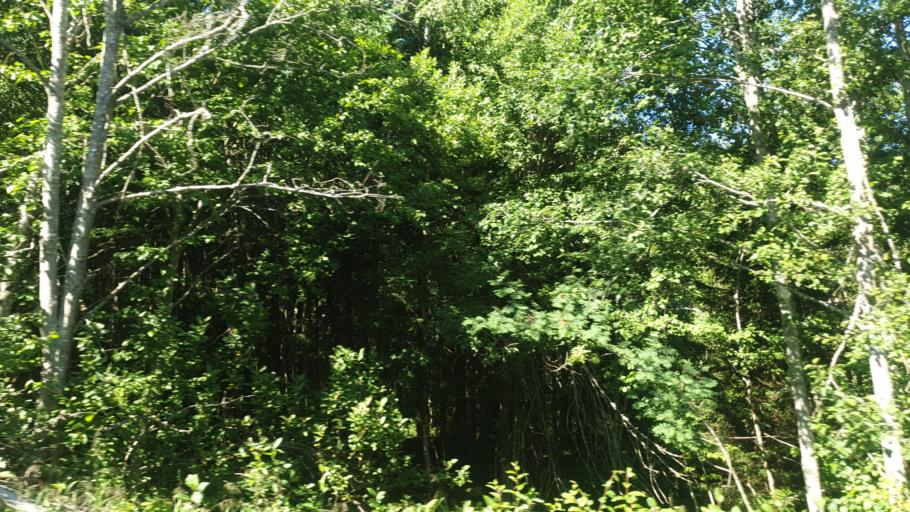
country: NO
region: Sor-Trondelag
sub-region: Meldal
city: Meldal
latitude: 63.1420
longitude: 9.7119
